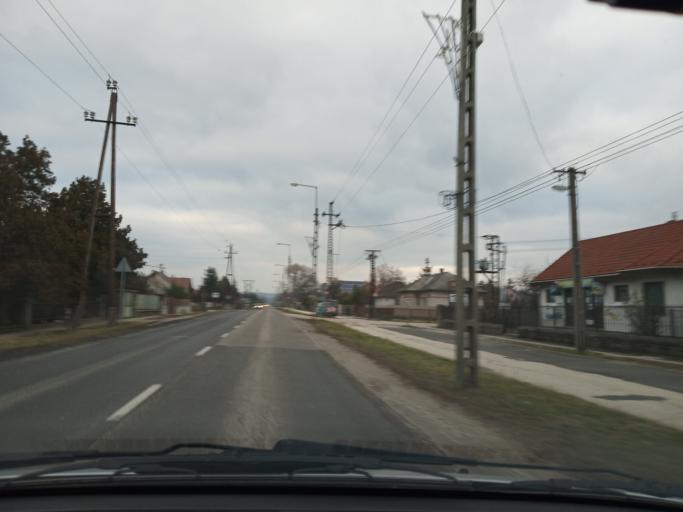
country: HU
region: Komarom-Esztergom
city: Dorog
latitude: 47.7433
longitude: 18.7284
